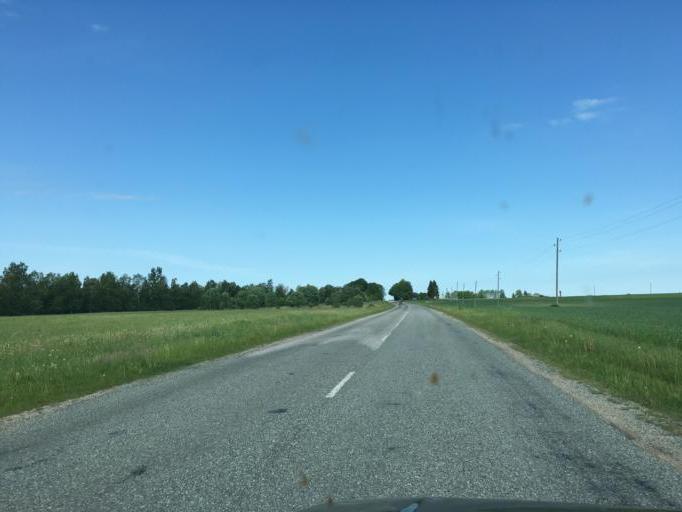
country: LV
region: Talsu Rajons
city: Valdemarpils
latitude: 57.3700
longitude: 22.4842
